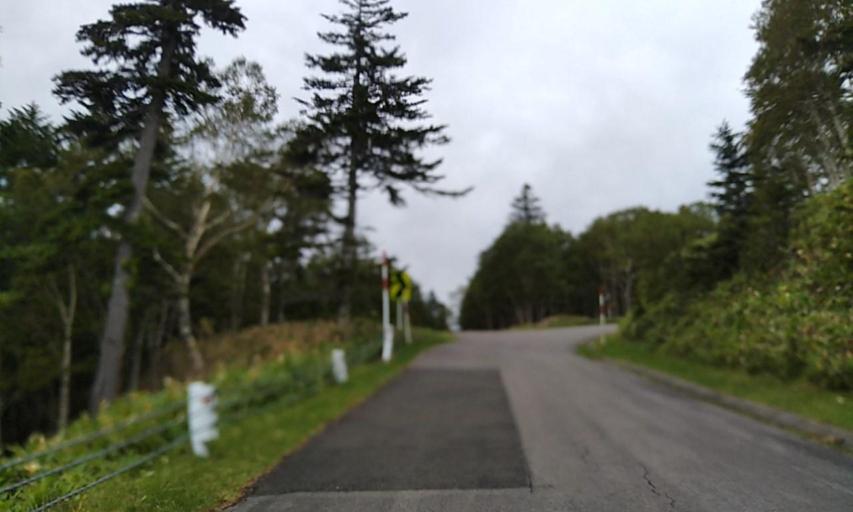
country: JP
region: Hokkaido
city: Bihoro
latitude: 43.5661
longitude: 144.2185
